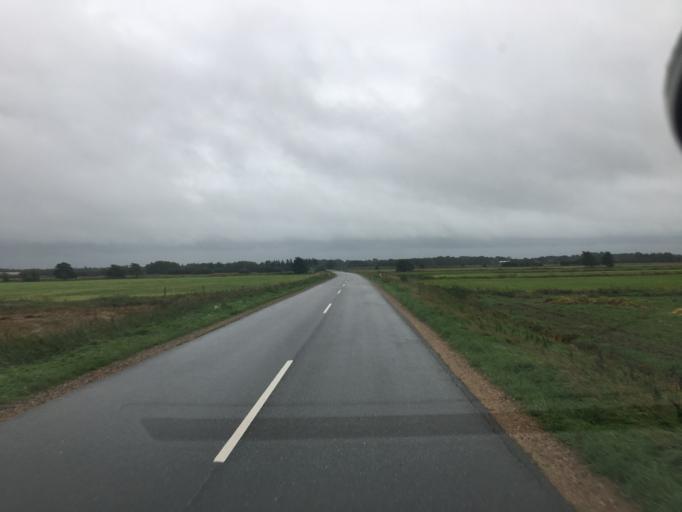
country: DE
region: Schleswig-Holstein
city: Bramstedtlund
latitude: 54.9698
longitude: 9.0453
